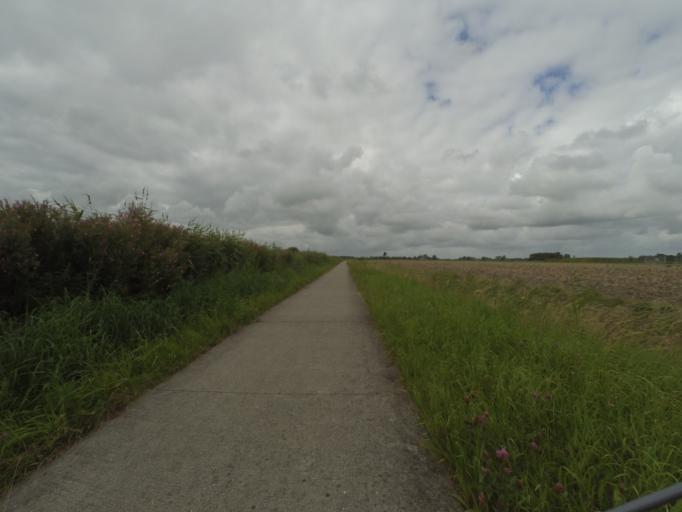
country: NL
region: Friesland
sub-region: Gemeente Kollumerland en Nieuwkruisland
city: Kollum
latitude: 53.3181
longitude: 6.1265
